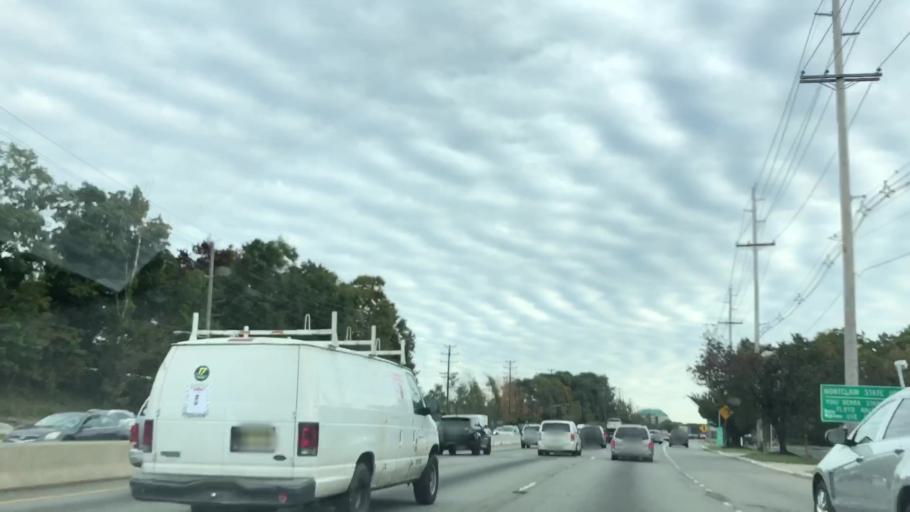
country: US
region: New Jersey
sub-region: Passaic County
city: Little Falls
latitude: 40.8802
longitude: -74.2067
